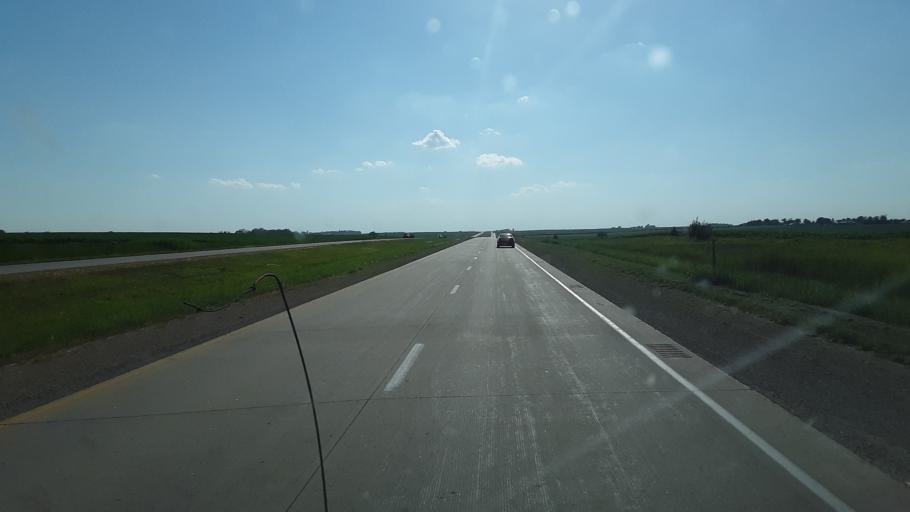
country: US
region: Iowa
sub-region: Grundy County
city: Dike
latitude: 42.4638
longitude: -92.6719
